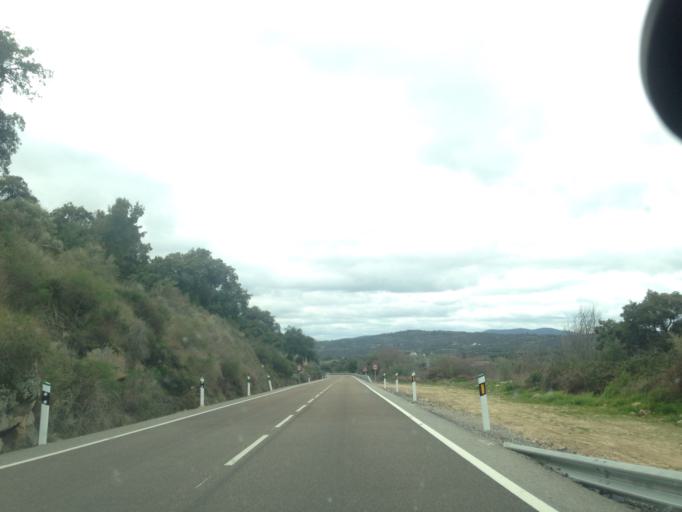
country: ES
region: Extremadura
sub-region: Provincia de Caceres
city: Montanchez
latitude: 39.2194
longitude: -6.1706
